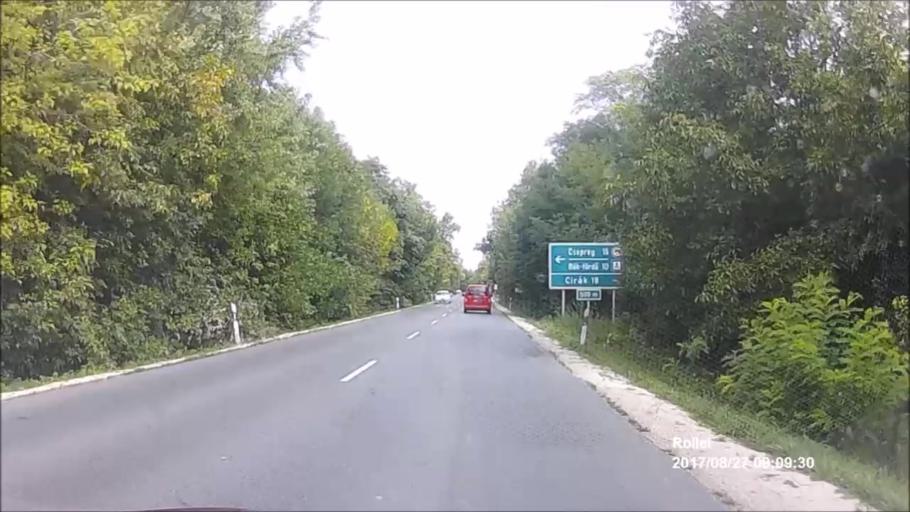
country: HU
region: Vas
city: Sarvar
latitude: 47.3740
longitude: 16.8848
